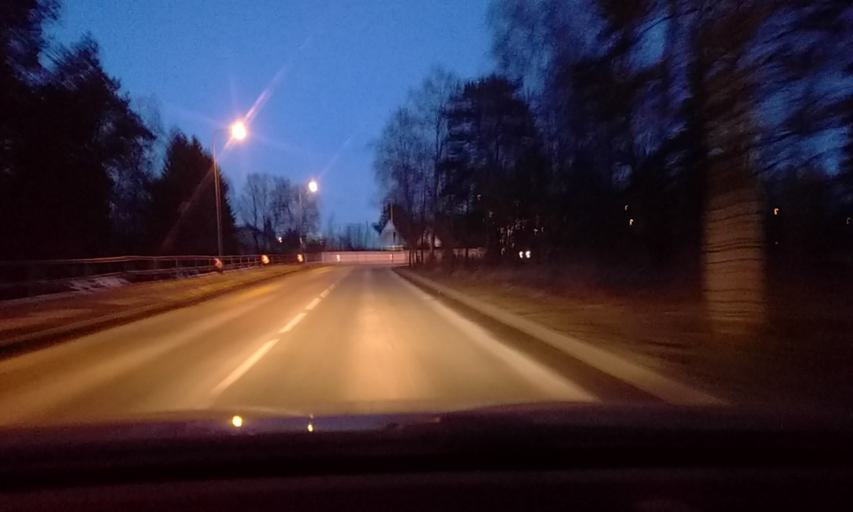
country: EE
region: Harju
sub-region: Viimsi vald
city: Viimsi
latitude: 59.4862
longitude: 24.8636
